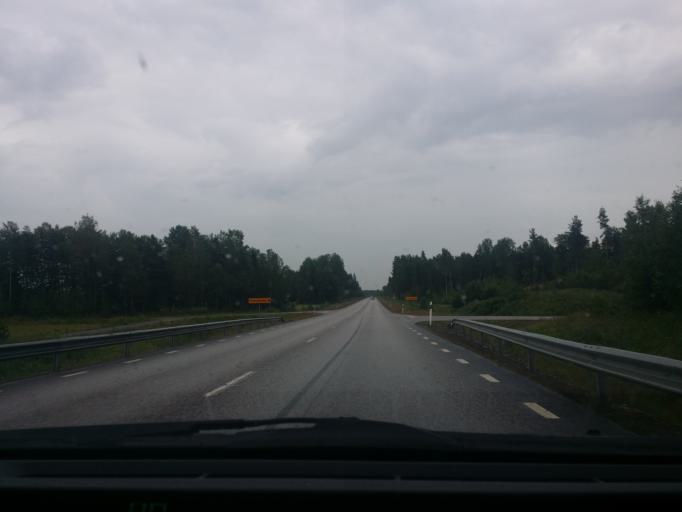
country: SE
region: OErebro
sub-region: Lindesbergs Kommun
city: Frovi
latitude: 59.4675
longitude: 15.4121
